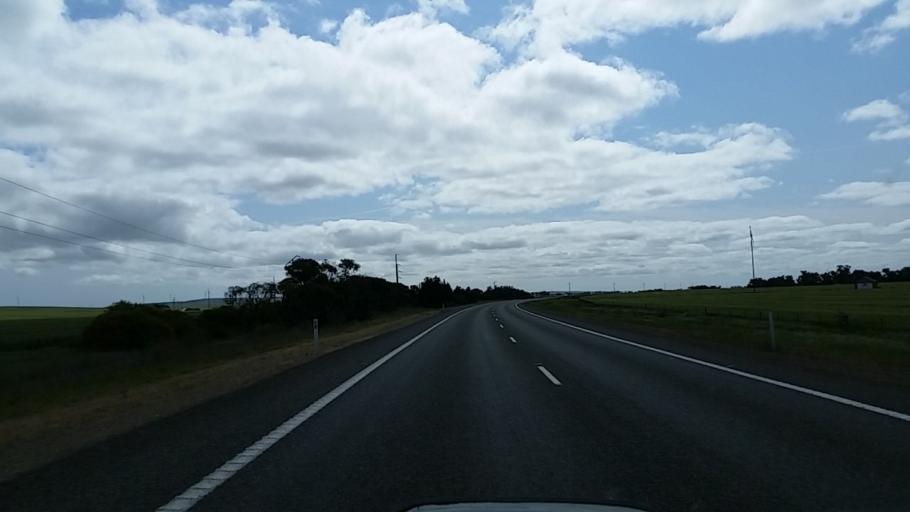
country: AU
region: South Australia
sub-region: Port Pirie City and Dists
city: Crystal Brook
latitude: -33.5182
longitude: 138.1923
